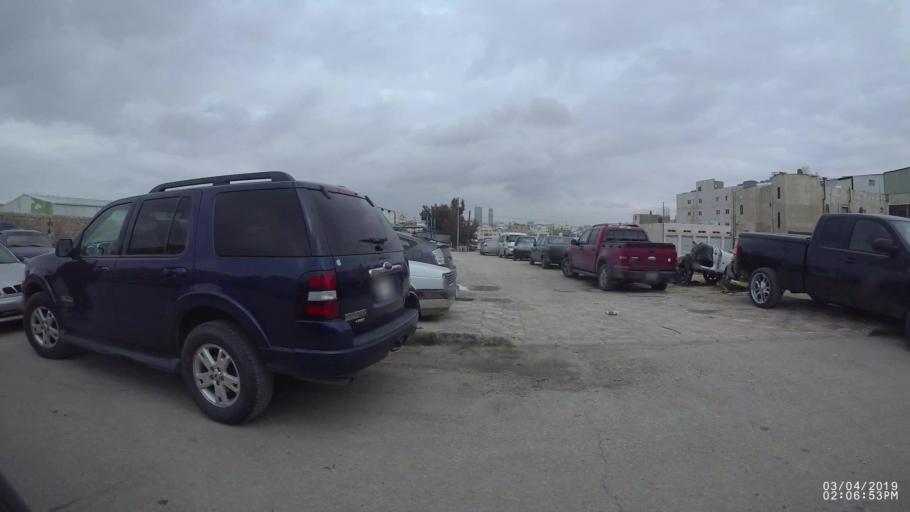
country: JO
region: Amman
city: Wadi as Sir
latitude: 31.9431
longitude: 35.8422
